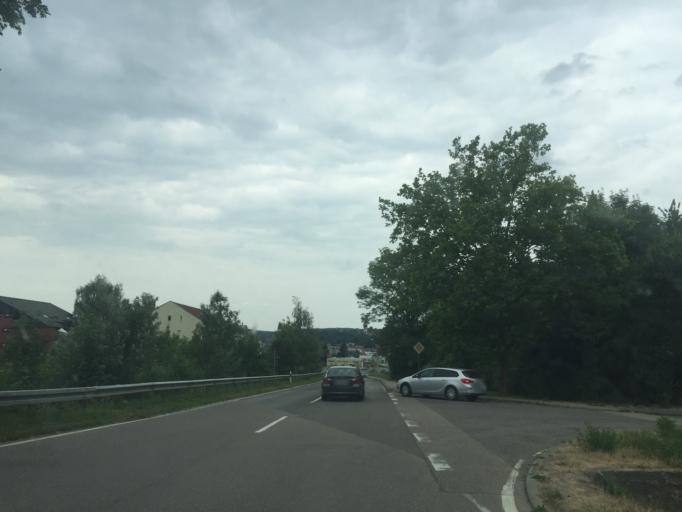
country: DE
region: Baden-Wuerttemberg
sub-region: Karlsruhe Region
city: Sinsheim
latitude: 49.2448
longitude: 8.8768
